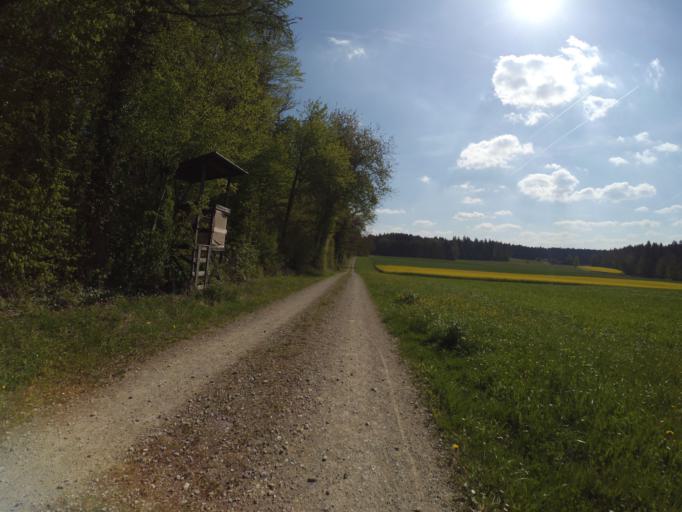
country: CH
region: Thurgau
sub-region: Frauenfeld District
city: Diessenhofen
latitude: 47.6568
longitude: 8.7519
